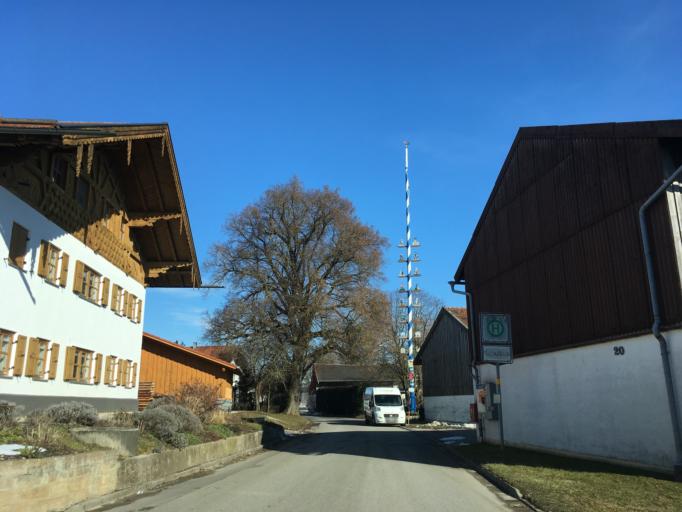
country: DE
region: Bavaria
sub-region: Upper Bavaria
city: Edling
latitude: 48.0718
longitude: 12.1587
